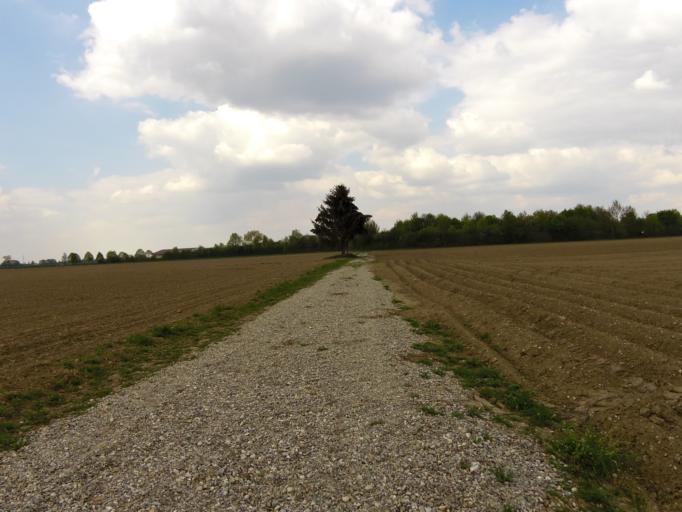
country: DE
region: Bavaria
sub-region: Upper Bavaria
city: Stammham
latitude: 48.3174
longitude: 11.8809
